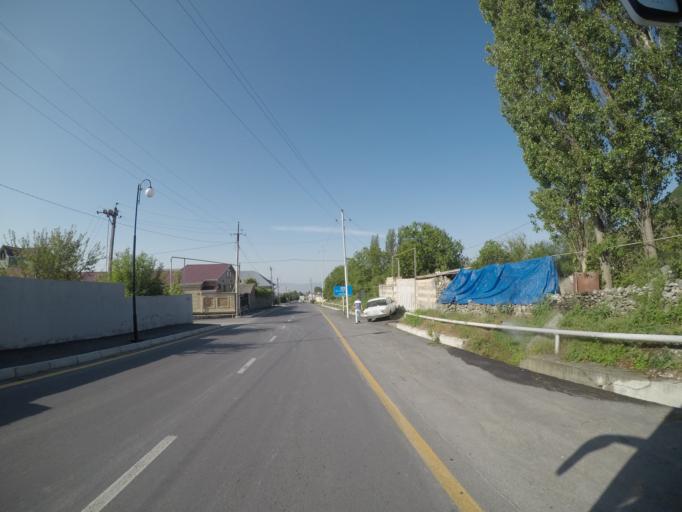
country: AZ
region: Shaki City
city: Sheki
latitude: 41.2175
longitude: 47.1690
